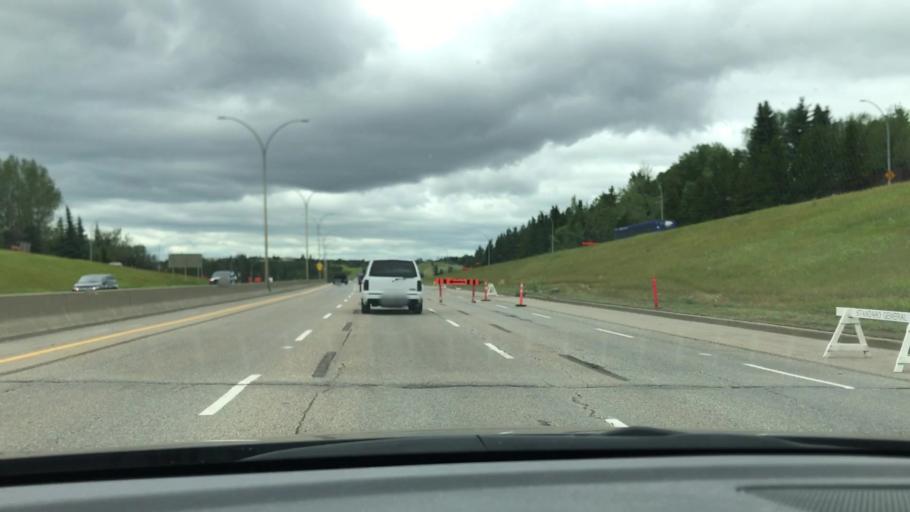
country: CA
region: Alberta
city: Edmonton
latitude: 53.4831
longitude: -113.5423
